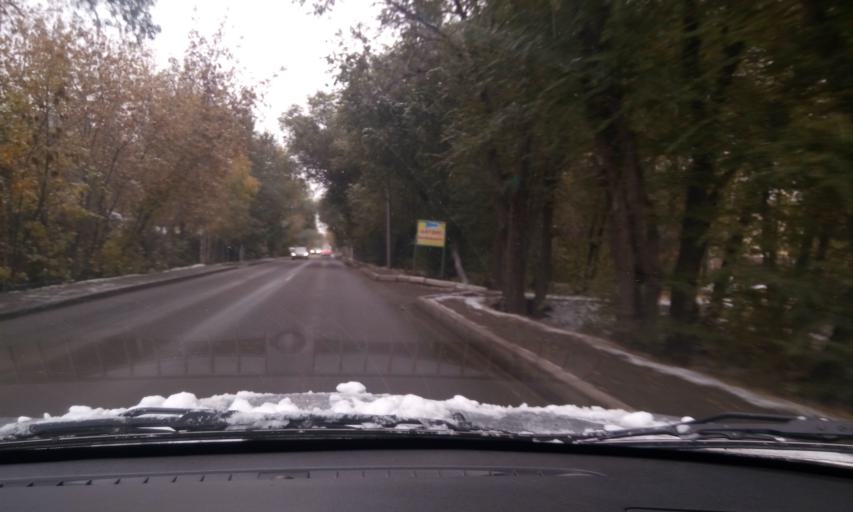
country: KZ
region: Astana Qalasy
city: Astana
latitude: 51.1396
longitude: 71.4331
